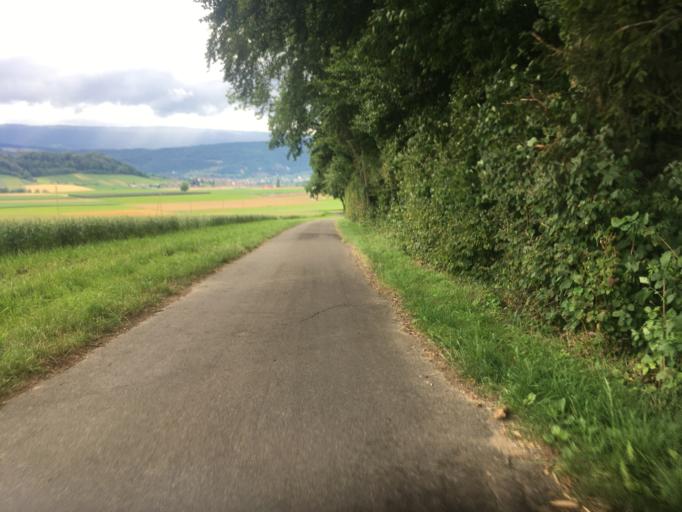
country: CH
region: Bern
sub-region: Seeland District
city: Ins
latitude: 47.0203
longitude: 7.1024
